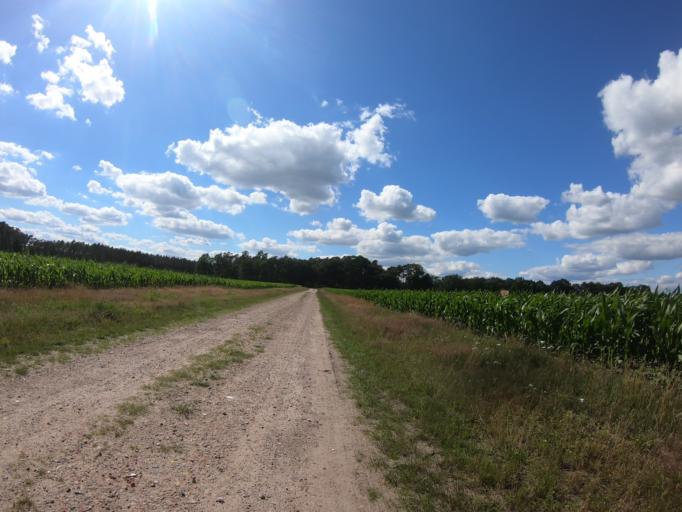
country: DE
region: Lower Saxony
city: Wagenhoff
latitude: 52.5040
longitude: 10.4765
